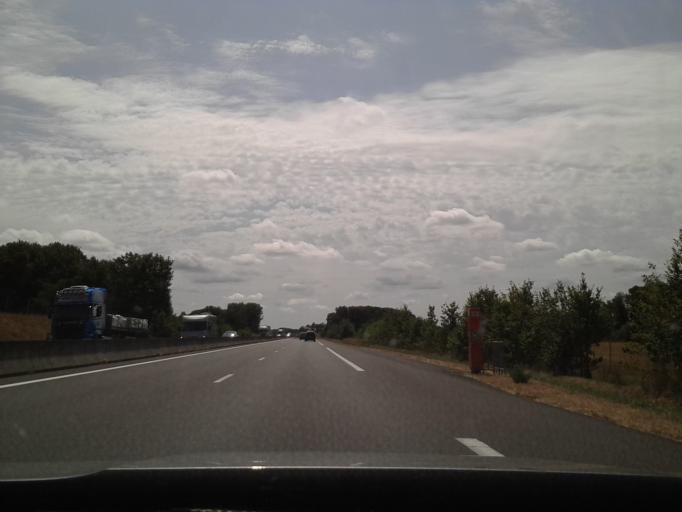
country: FR
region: Centre
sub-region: Departement d'Indre-et-Loire
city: Saint-Antoine-du-Rocher
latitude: 47.5095
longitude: 0.6356
